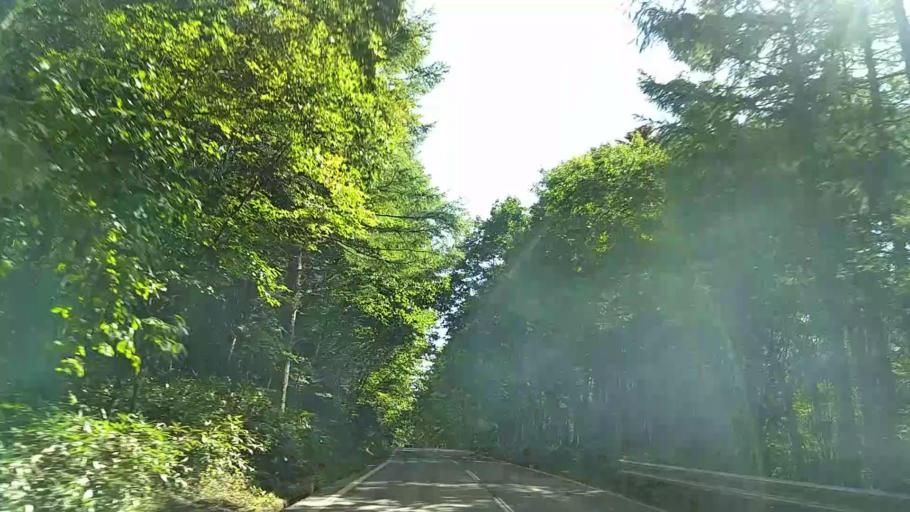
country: JP
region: Nagano
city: Chino
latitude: 36.1119
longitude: 138.2727
